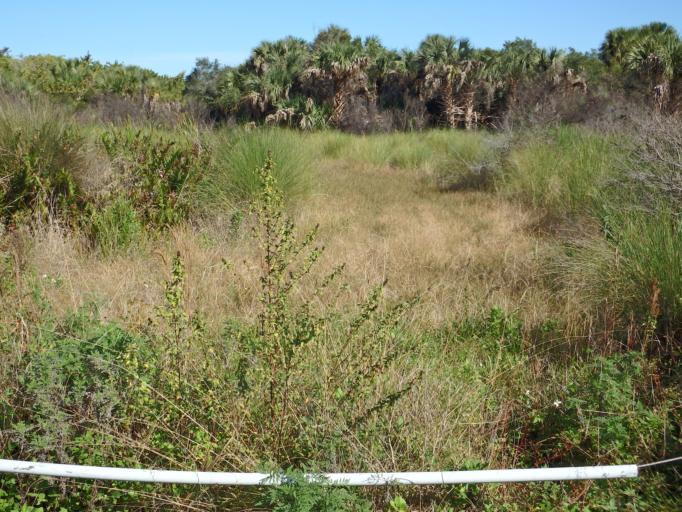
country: US
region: Florida
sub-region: Lee County
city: Saint James City
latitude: 26.4541
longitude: -82.1376
